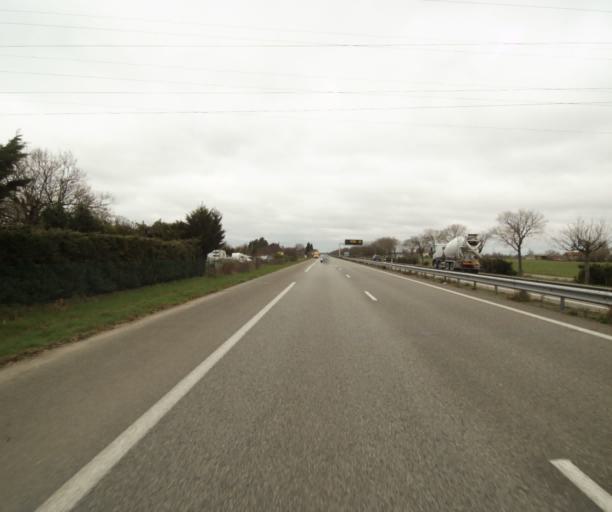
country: FR
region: Midi-Pyrenees
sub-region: Departement de l'Ariege
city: La Tour-du-Crieu
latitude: 43.1199
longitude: 1.6296
